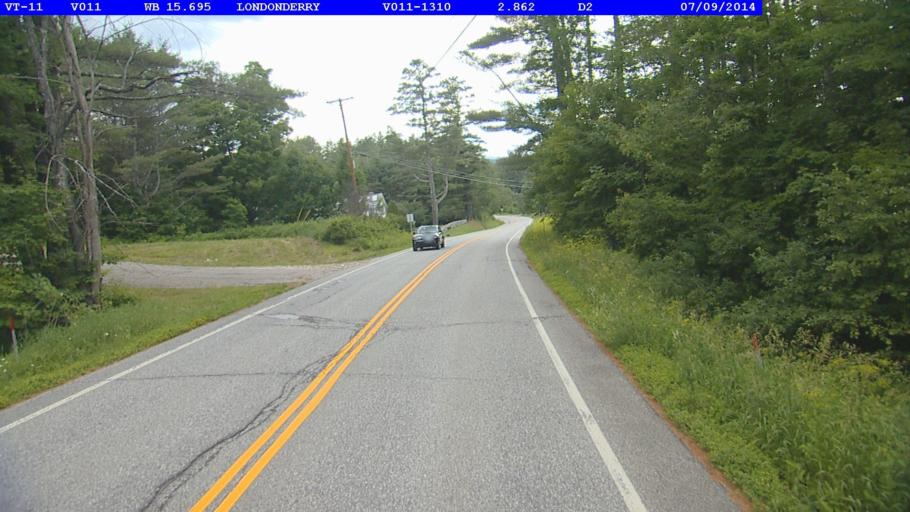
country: US
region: Vermont
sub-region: Windsor County
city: Chester
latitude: 43.2239
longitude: -72.7988
